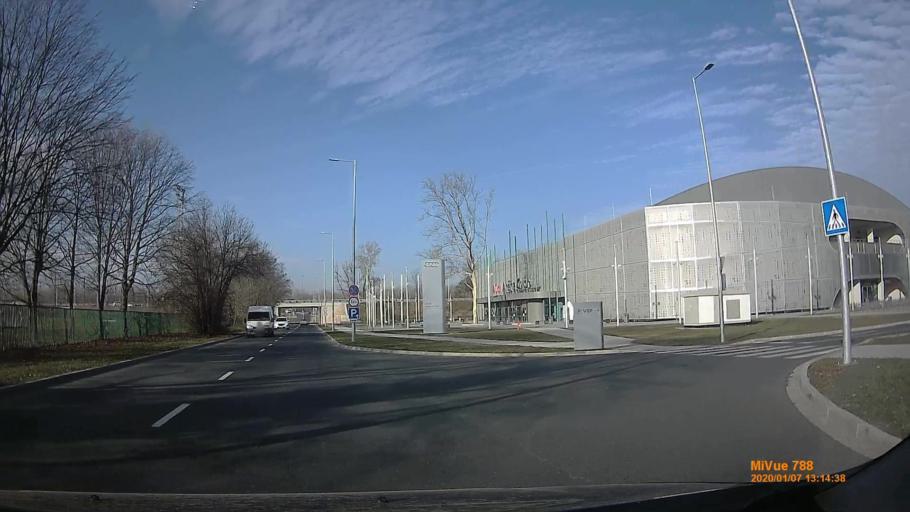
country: HU
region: Gyor-Moson-Sopron
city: Gyor
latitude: 47.6974
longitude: 17.6669
